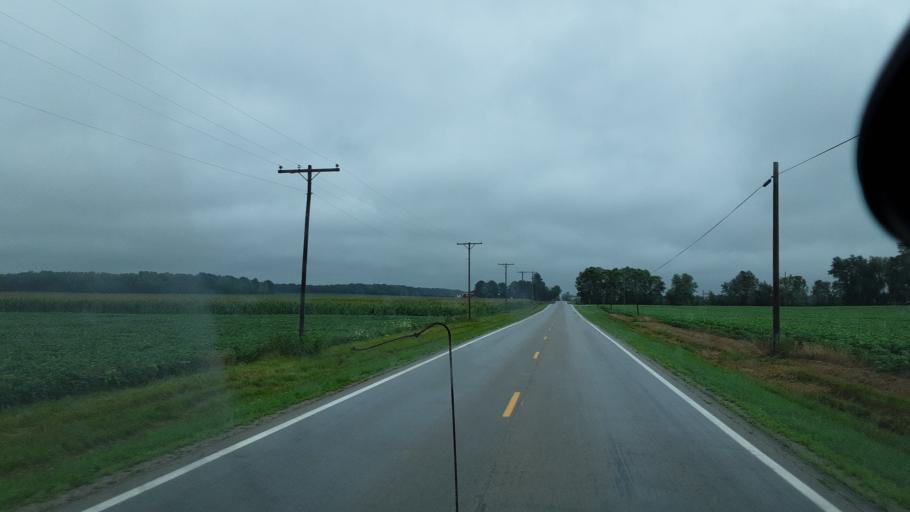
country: US
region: Ohio
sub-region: Mercer County
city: Rockford
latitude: 40.7426
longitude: -84.7431
